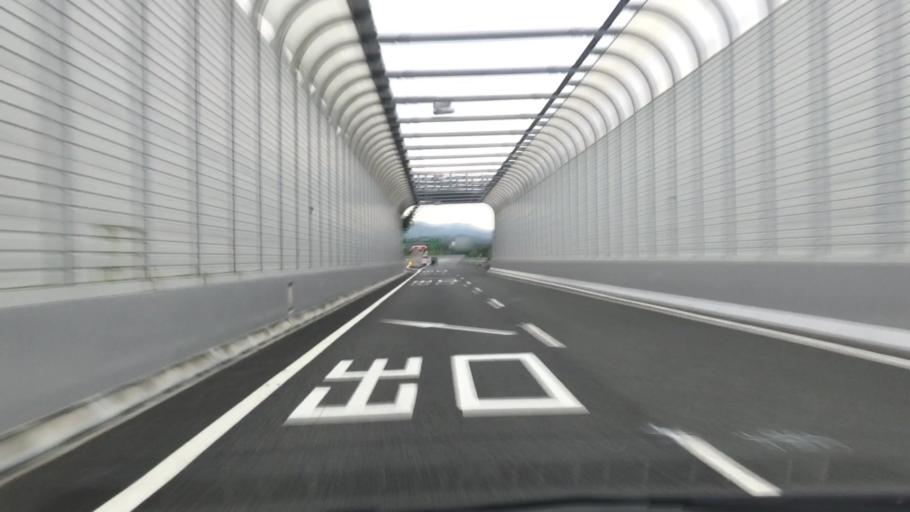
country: JP
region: Hyogo
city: Sandacho
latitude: 34.8191
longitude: 135.2560
